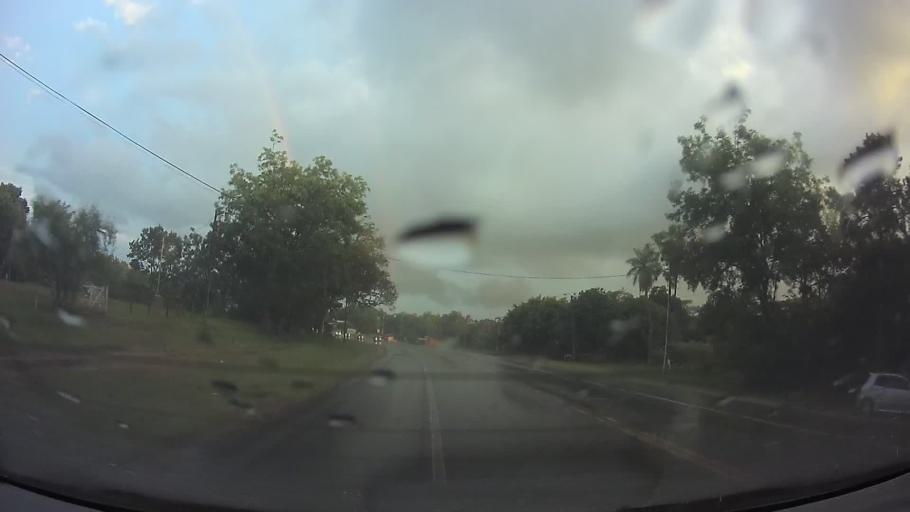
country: PY
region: Paraguari
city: Paraguari
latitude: -25.5955
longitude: -57.2161
